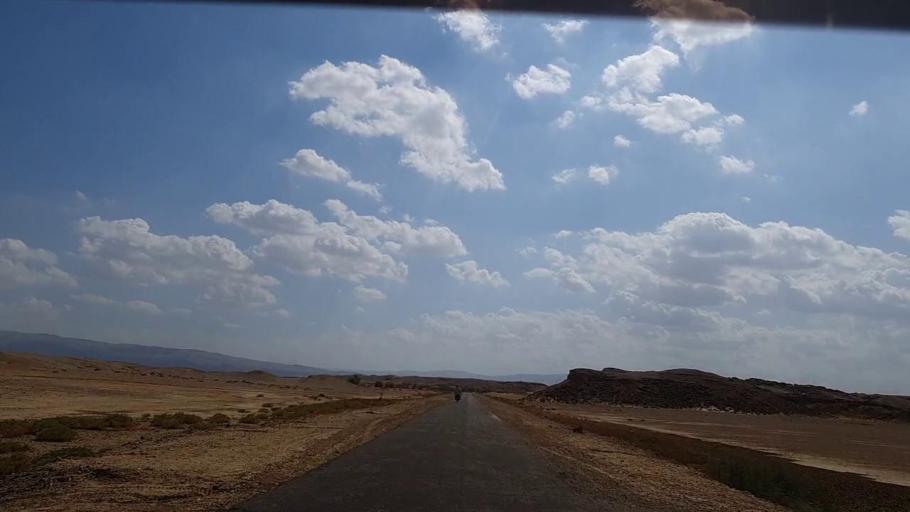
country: PK
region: Sindh
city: Johi
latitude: 26.5254
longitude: 67.5107
